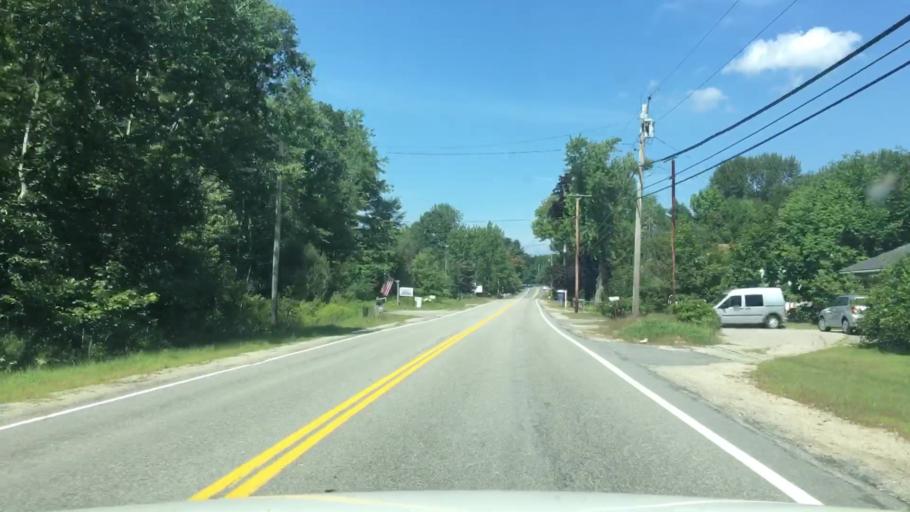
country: US
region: Maine
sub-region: Cumberland County
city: Falmouth
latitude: 43.7499
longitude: -70.2989
